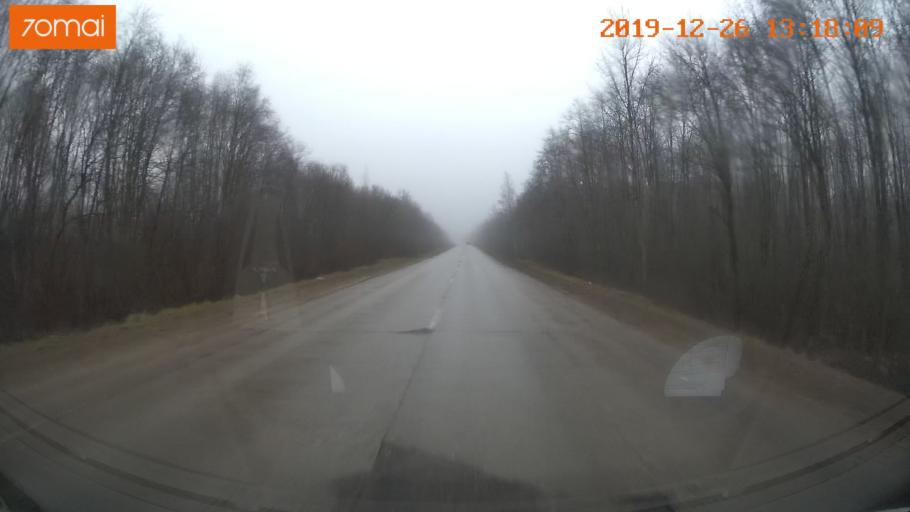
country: RU
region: Vologda
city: Cherepovets
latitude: 58.9593
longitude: 38.1202
